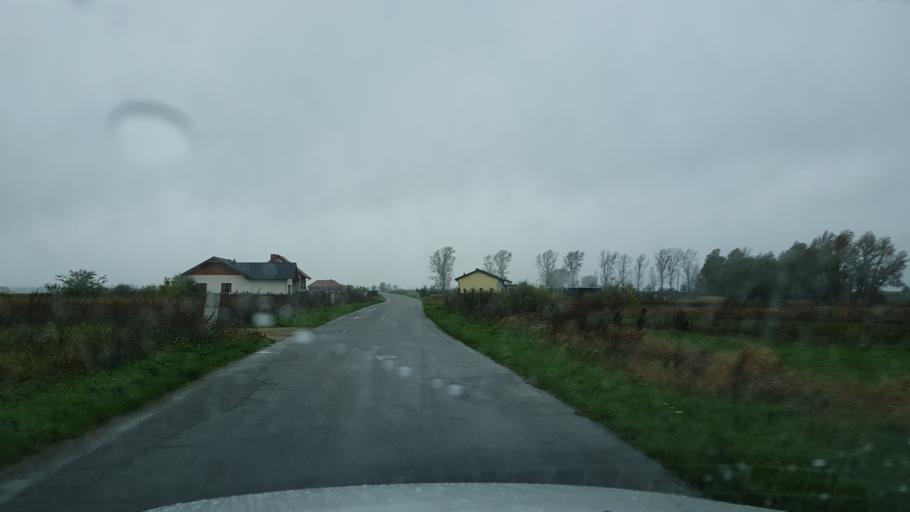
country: PL
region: West Pomeranian Voivodeship
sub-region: Powiat pyrzycki
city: Kozielice
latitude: 53.1623
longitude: 14.8363
